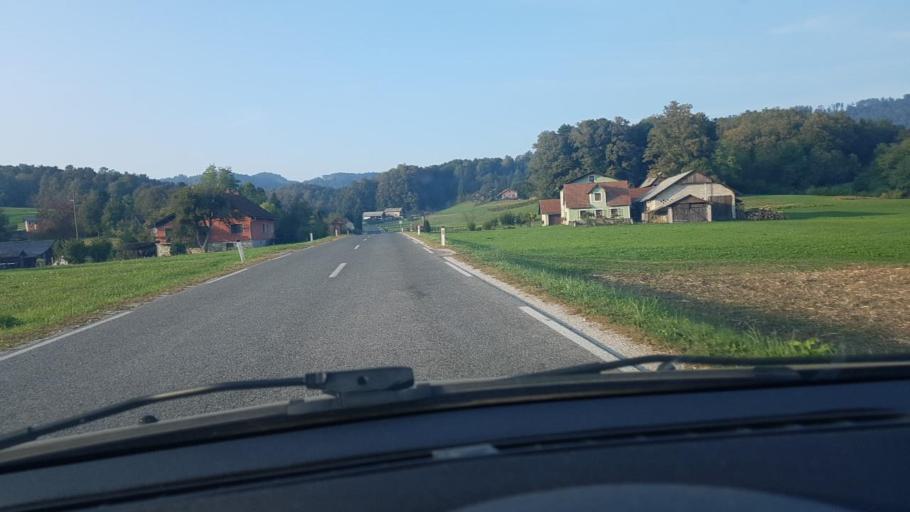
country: SI
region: Rogatec
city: Rogatec
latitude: 46.2423
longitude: 15.7015
